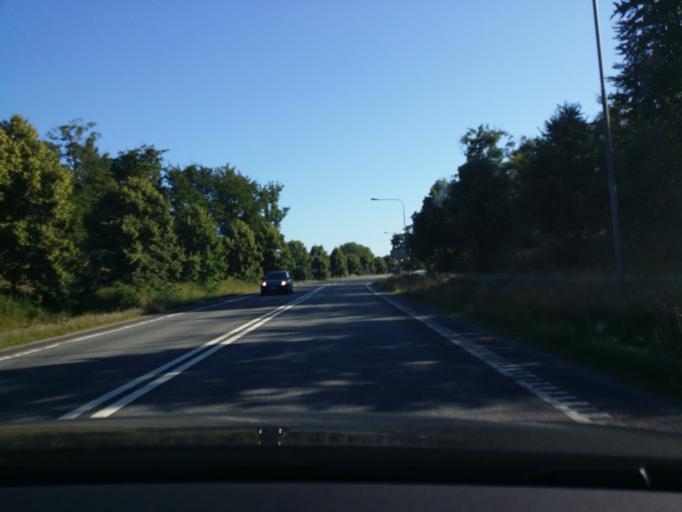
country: SE
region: Blekinge
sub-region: Solvesborgs Kommun
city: Soelvesborg
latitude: 56.0629
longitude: 14.5970
